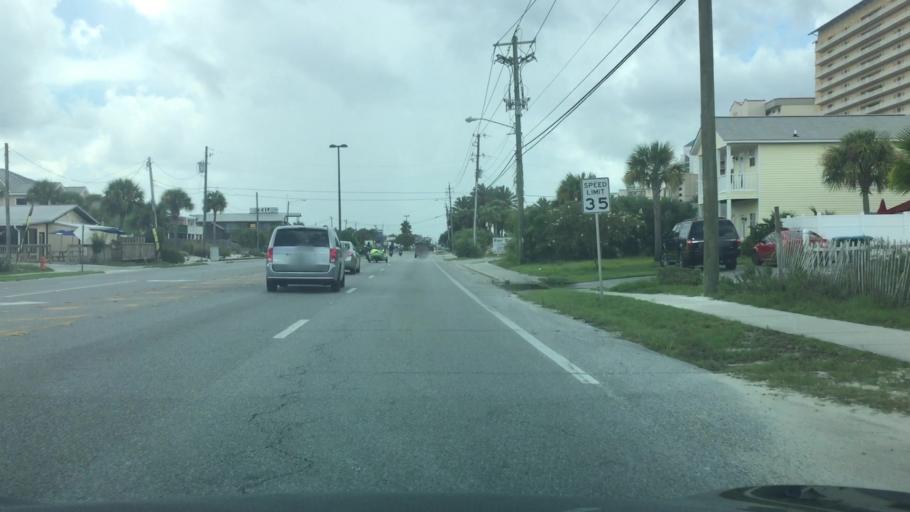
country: US
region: Florida
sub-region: Bay County
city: Lower Grand Lagoon
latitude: 30.1553
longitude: -85.7707
